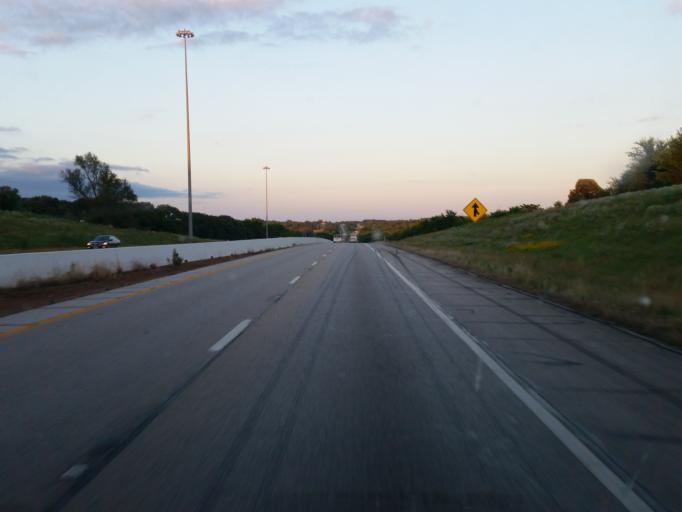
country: US
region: Texas
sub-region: Smith County
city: Hideaway
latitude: 32.4835
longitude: -95.5226
